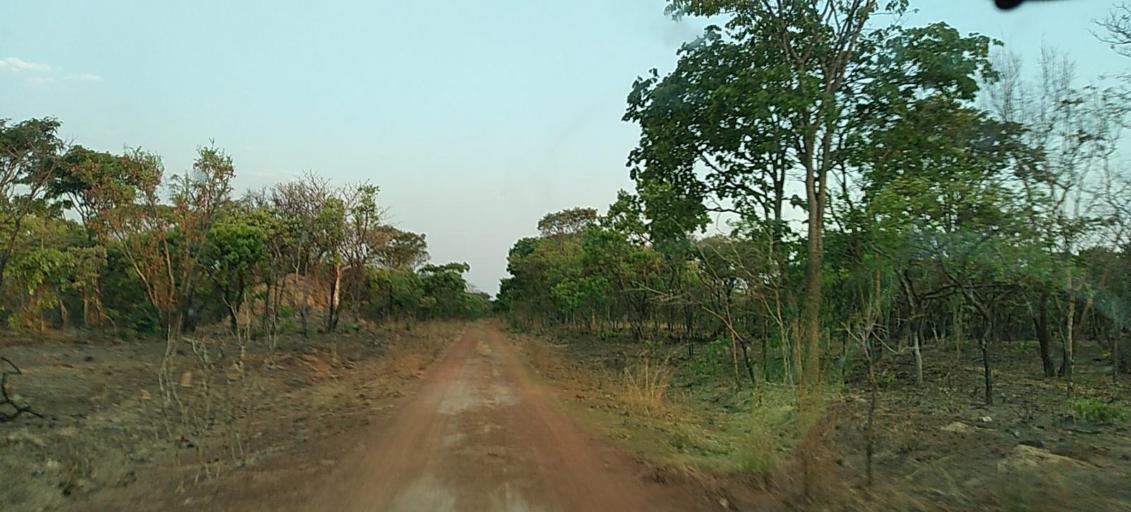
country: ZM
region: North-Western
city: Kalengwa
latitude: -13.1190
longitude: 25.1749
